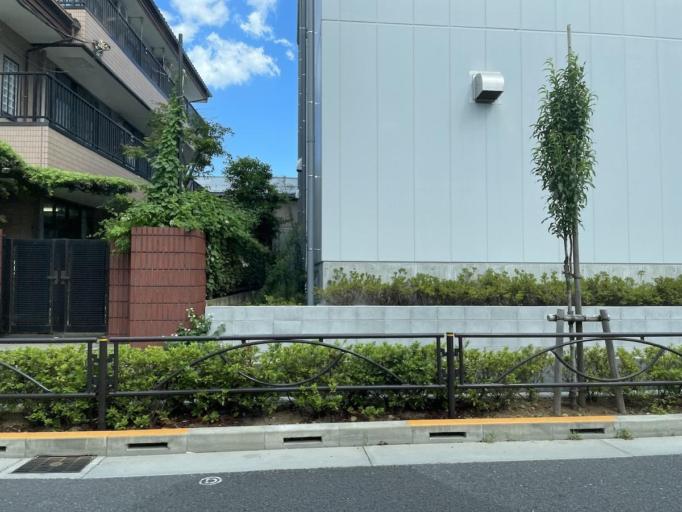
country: JP
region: Tokyo
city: Urayasu
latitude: 35.7205
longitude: 139.8304
